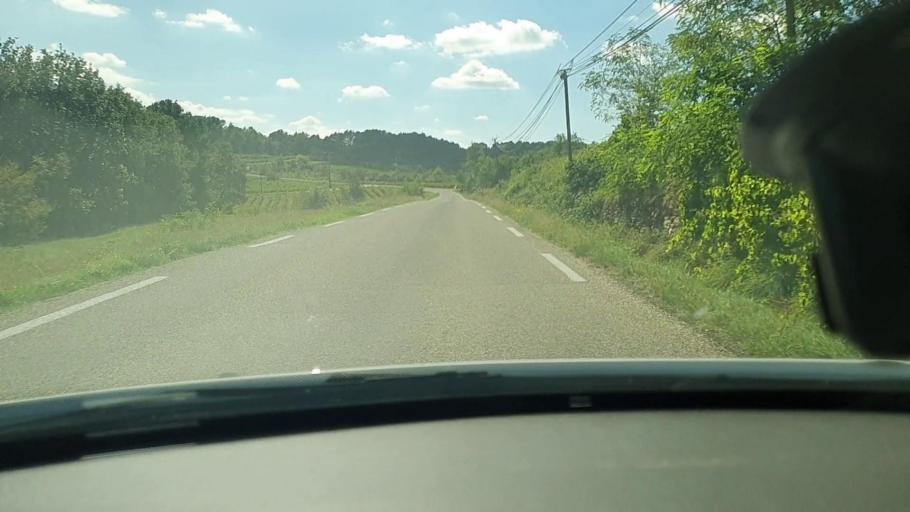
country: FR
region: Languedoc-Roussillon
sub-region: Departement du Gard
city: Goudargues
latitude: 44.1581
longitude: 4.4864
